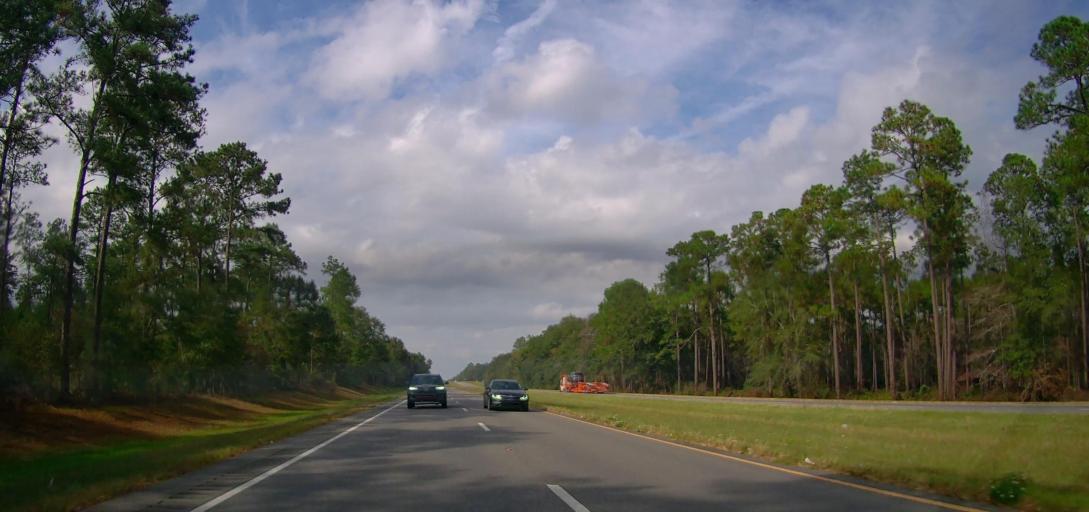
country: US
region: Georgia
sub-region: Thomas County
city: Meigs
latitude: 31.0030
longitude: -84.0494
